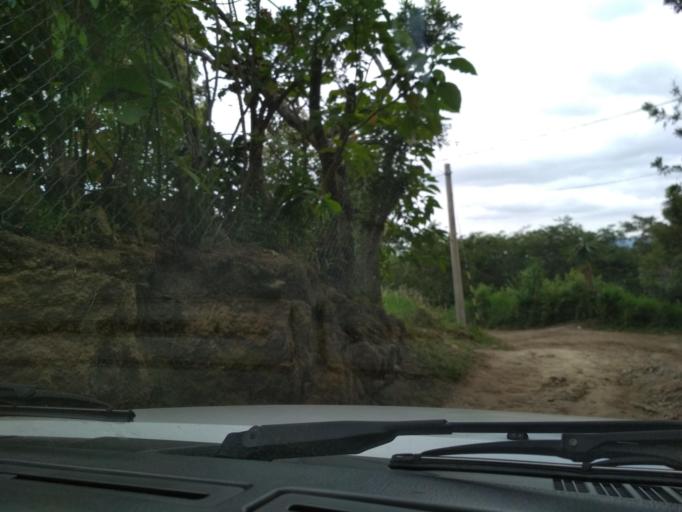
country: MX
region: Veracruz
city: El Castillo
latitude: 19.5789
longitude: -96.8580
